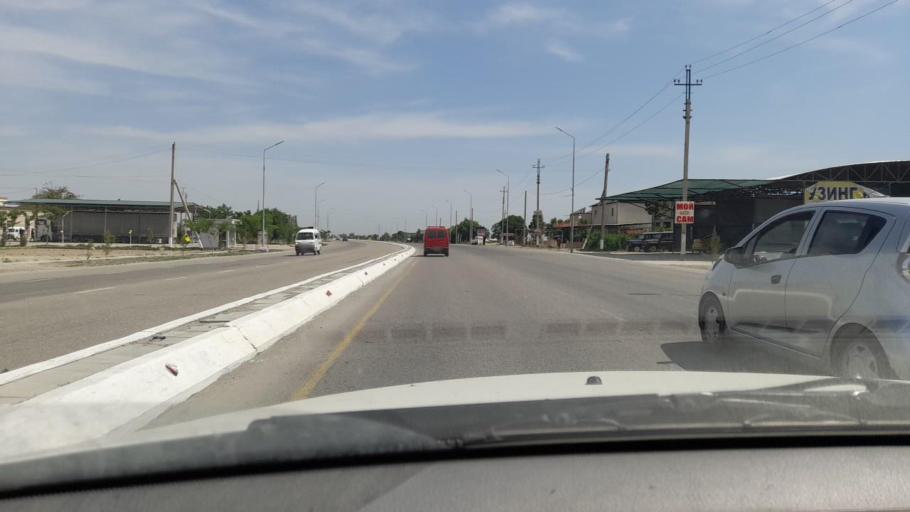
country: UZ
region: Bukhara
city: Galaosiyo
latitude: 39.8653
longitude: 64.4486
